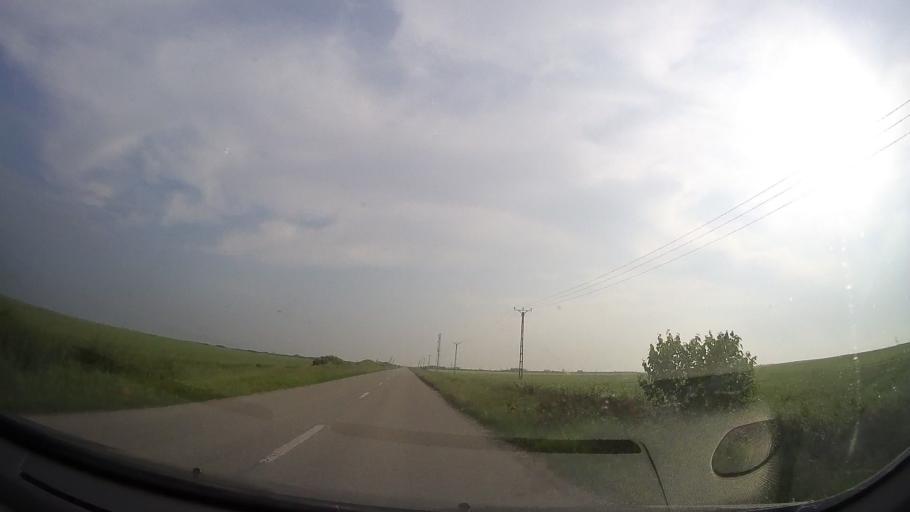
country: RO
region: Timis
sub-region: Comuna Foeni
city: Foeni
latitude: 45.5122
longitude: 20.8927
